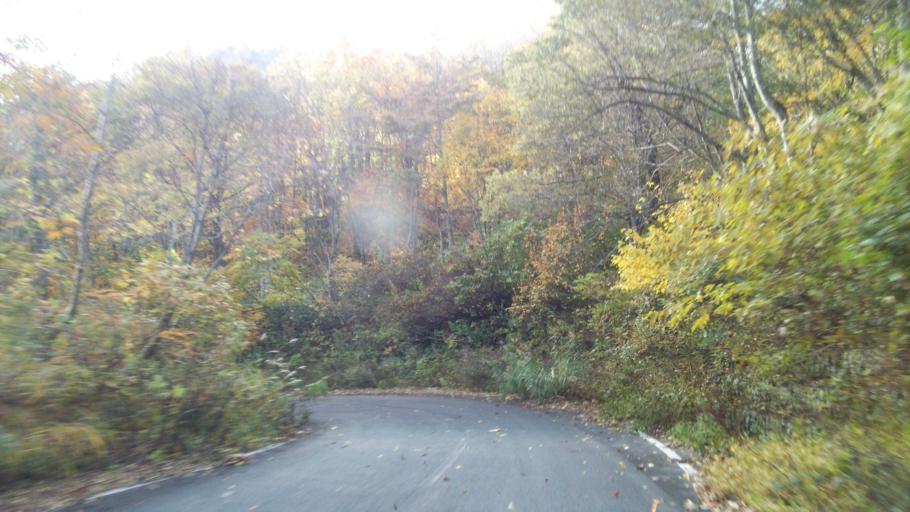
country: JP
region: Fukushima
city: Kitakata
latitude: 37.3841
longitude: 139.7331
